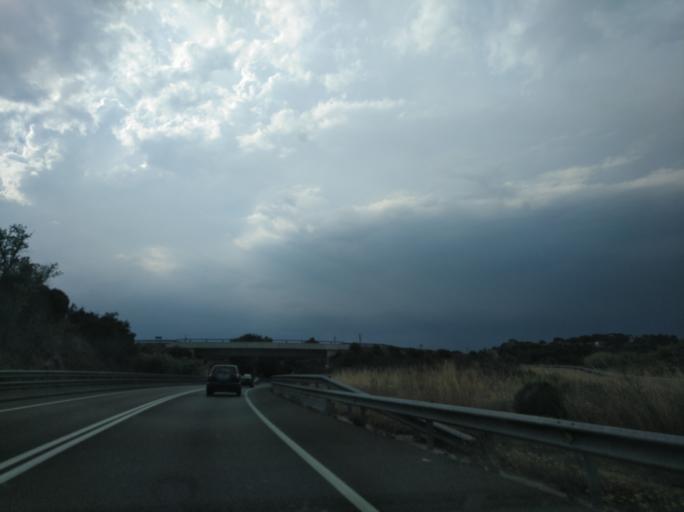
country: ES
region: Catalonia
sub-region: Provincia de Barcelona
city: Palafolls
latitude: 41.6702
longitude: 2.7273
